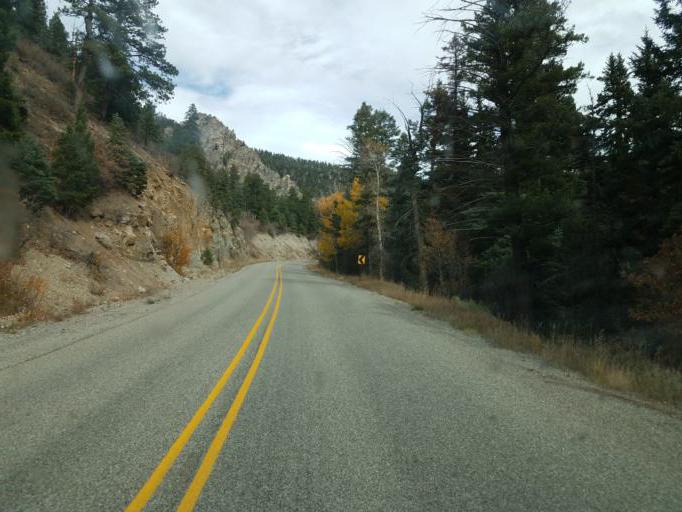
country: US
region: New Mexico
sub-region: Taos County
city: Arroyo Seco
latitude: 36.5550
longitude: -105.5380
